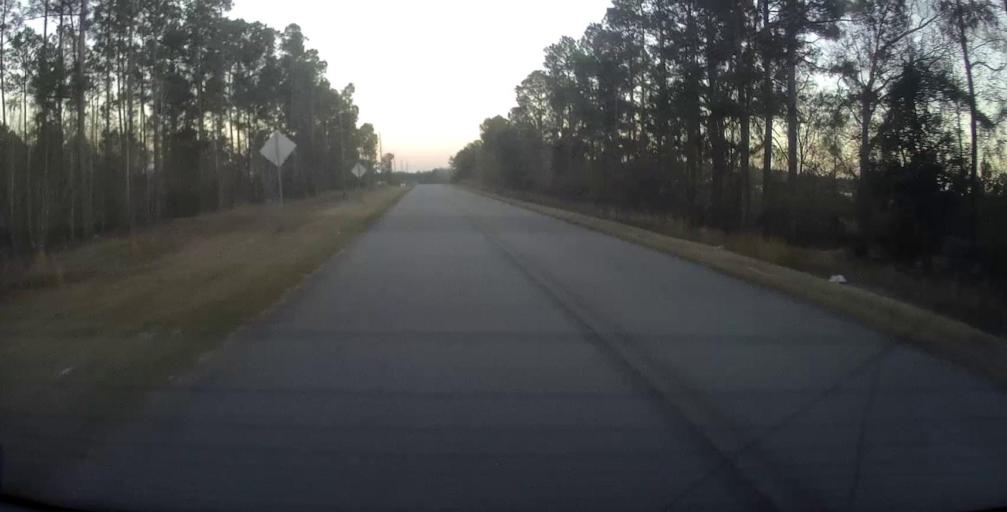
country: US
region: Georgia
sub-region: Dodge County
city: Eastman
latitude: 32.1685
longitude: -83.1544
